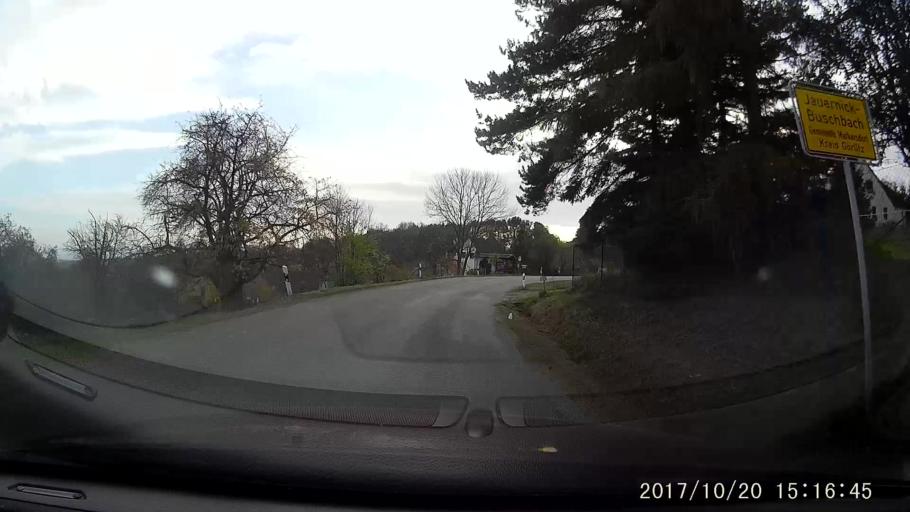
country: DE
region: Saxony
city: Schonau-Berzdorf
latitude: 51.0968
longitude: 14.9153
